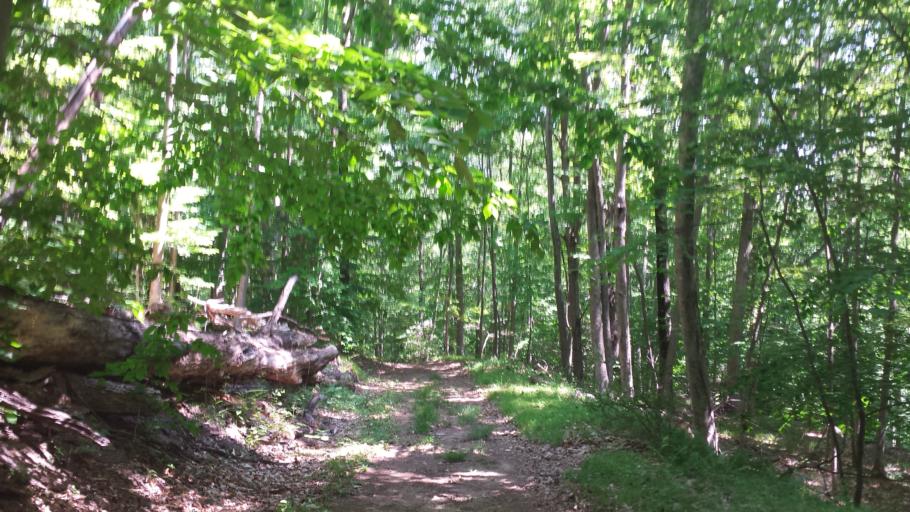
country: US
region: New York
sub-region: Westchester County
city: Pound Ridge
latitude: 41.2535
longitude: -73.5691
